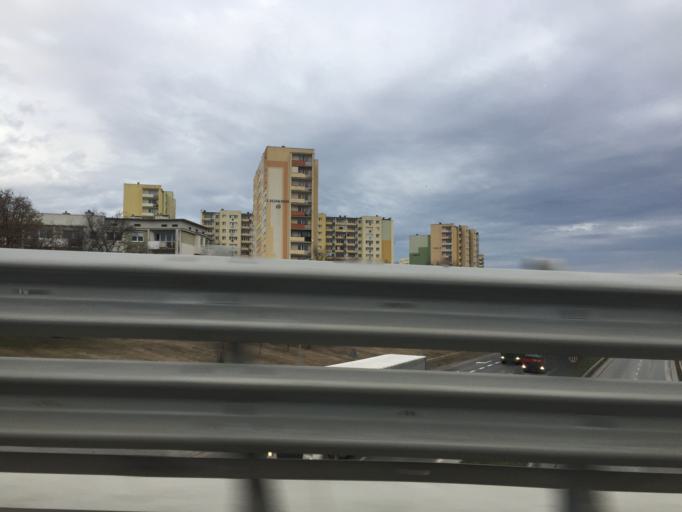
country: PL
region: Kujawsko-Pomorskie
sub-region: Bydgoszcz
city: Bydgoszcz
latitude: 53.1104
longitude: 18.0167
